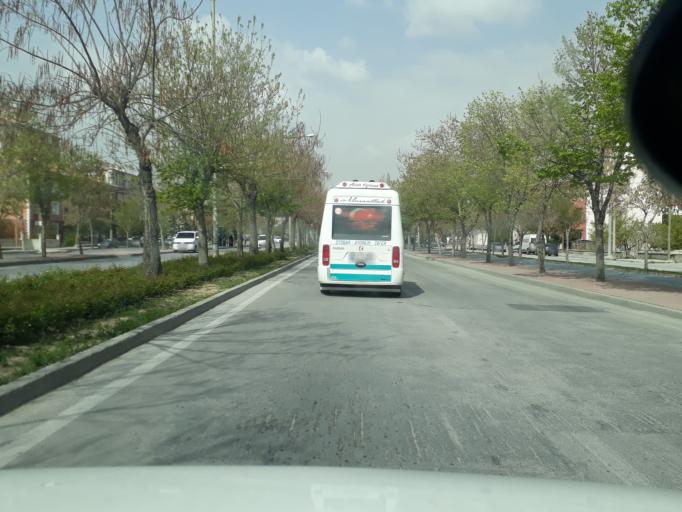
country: TR
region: Konya
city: Selcuklu
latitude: 37.9372
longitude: 32.4954
